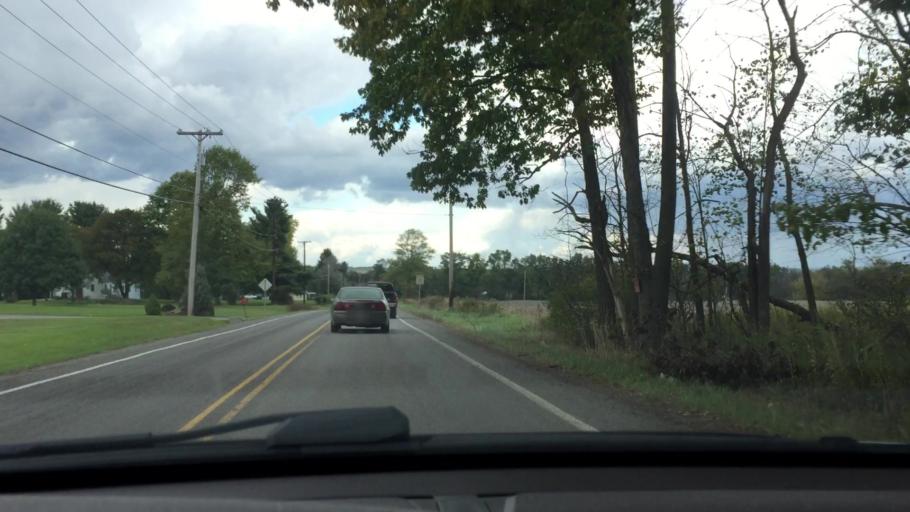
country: US
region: Pennsylvania
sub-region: Lawrence County
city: Oakwood
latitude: 40.9972
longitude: -80.4372
